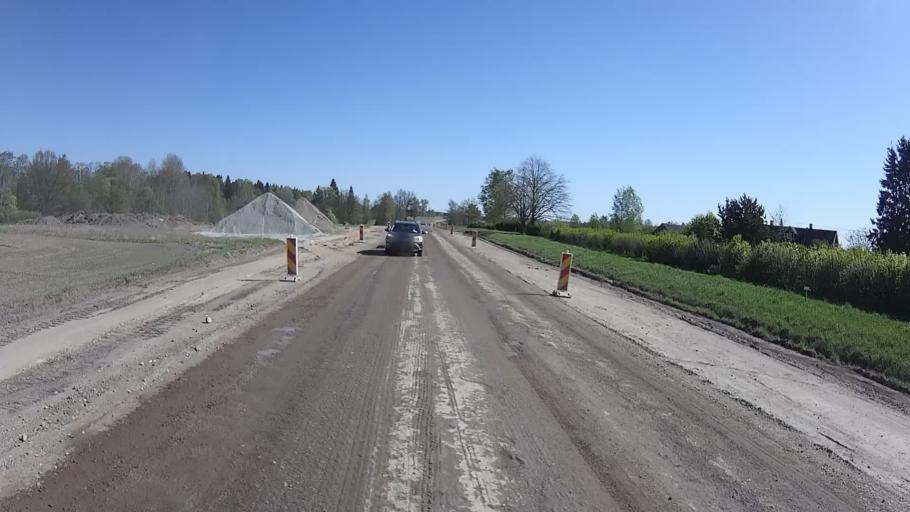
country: EE
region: Paernumaa
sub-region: Sindi linn
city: Sindi
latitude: 58.4398
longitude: 24.7443
